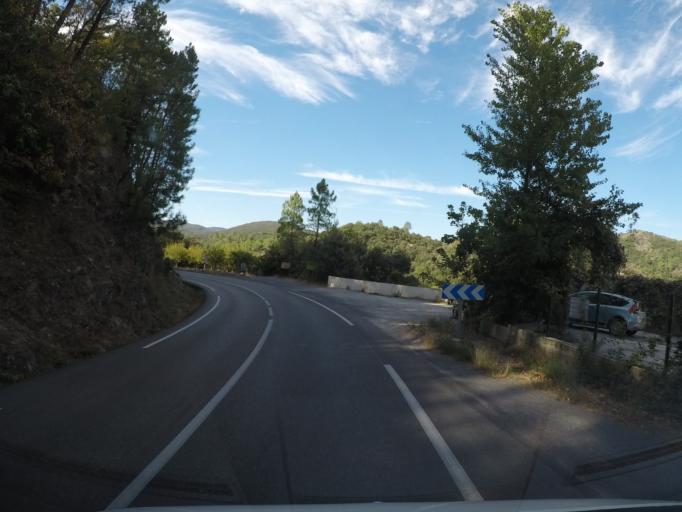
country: FR
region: Languedoc-Roussillon
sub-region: Departement du Gard
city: Anduze
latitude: 44.0730
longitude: 3.9684
